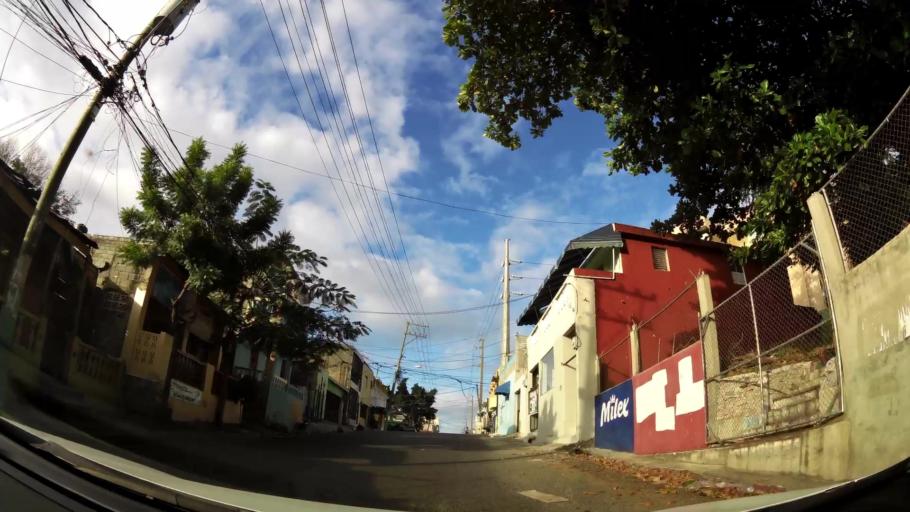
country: DO
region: Nacional
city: San Carlos
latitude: 18.4799
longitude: -69.8860
